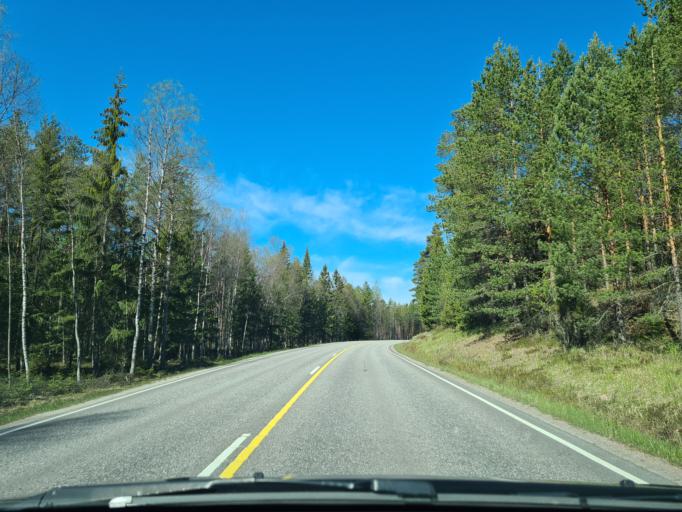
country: FI
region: Uusimaa
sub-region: Helsinki
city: Vihti
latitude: 60.3918
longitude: 24.4932
